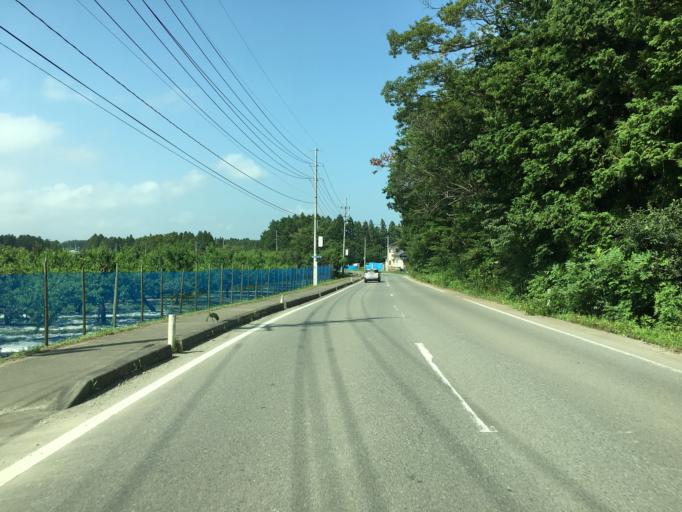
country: JP
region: Miyagi
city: Marumori
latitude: 37.8534
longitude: 140.8957
